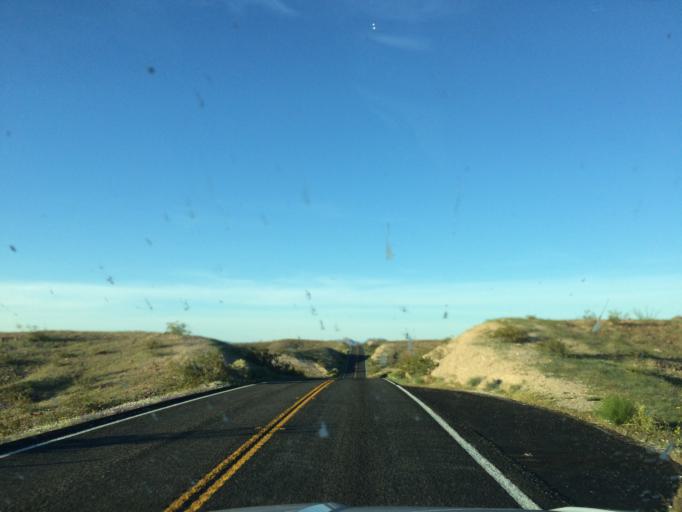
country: US
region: California
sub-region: Riverside County
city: Mesa Verde
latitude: 33.1985
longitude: -114.8584
